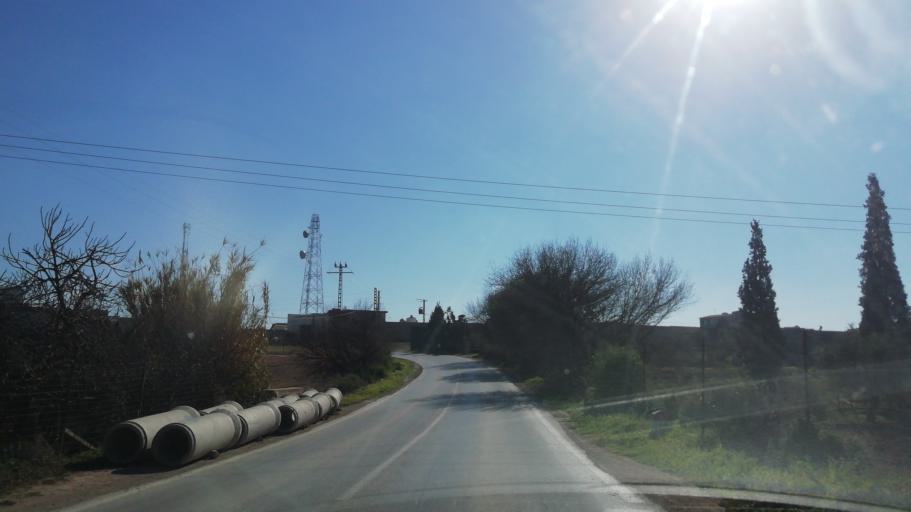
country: DZ
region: Tlemcen
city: Nedroma
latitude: 34.8378
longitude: -1.7028
